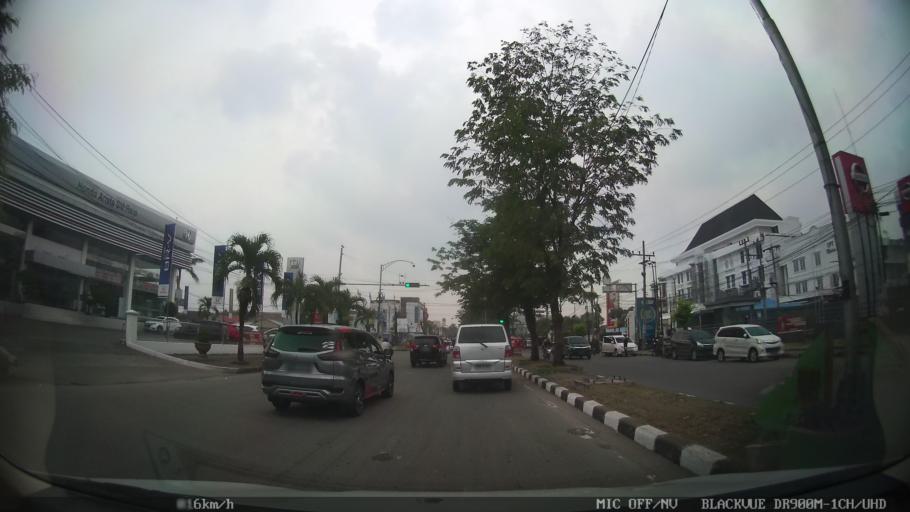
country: ID
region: North Sumatra
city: Deli Tua
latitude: 3.5455
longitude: 98.6986
